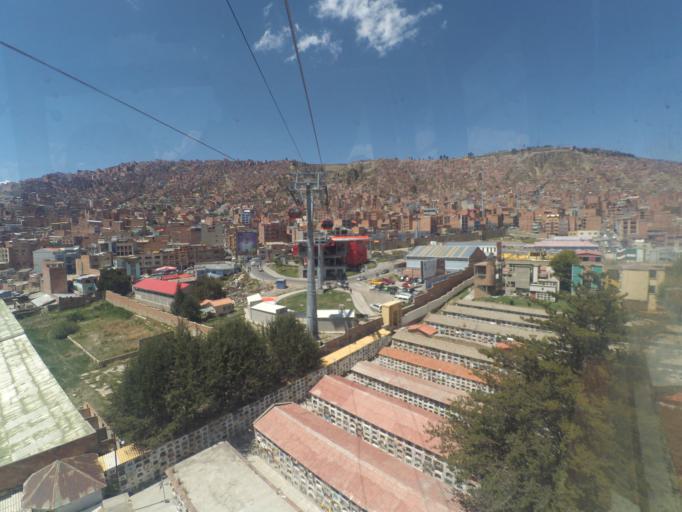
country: BO
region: La Paz
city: La Paz
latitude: -16.4972
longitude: -68.1517
